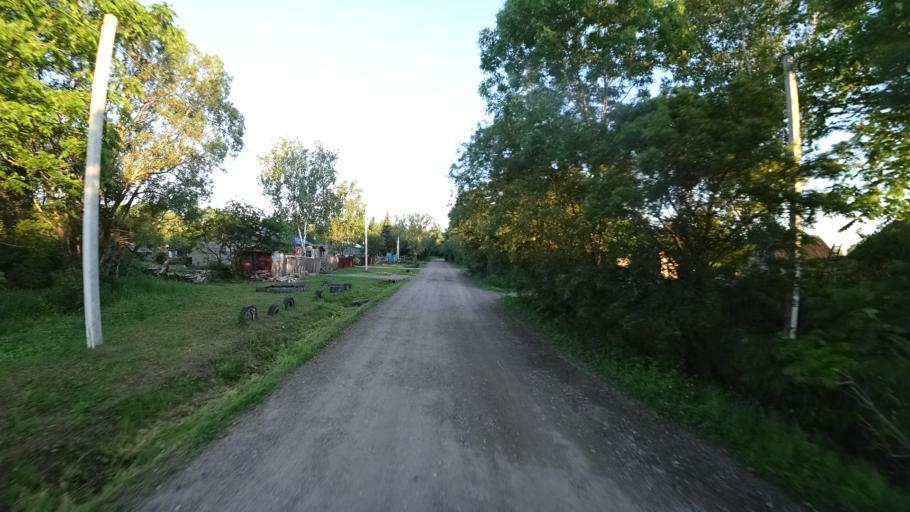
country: RU
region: Khabarovsk Krai
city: Khor
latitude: 47.8511
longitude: 134.9835
